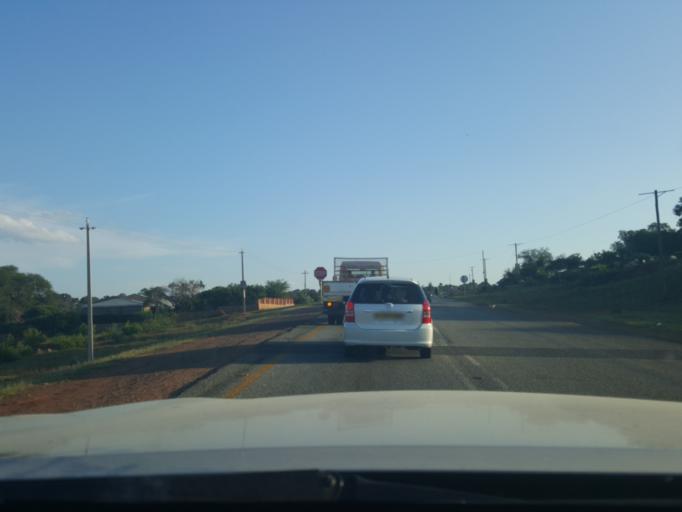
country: ZA
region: North-West
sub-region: Ngaka Modiri Molema District Municipality
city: Zeerust
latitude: -25.3257
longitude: 26.1216
